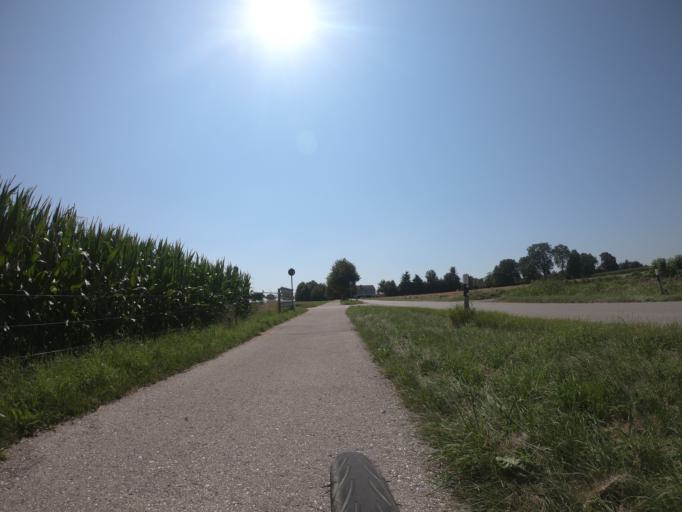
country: DE
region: Bavaria
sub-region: Upper Bavaria
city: Fuerstenfeldbruck
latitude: 48.1558
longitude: 11.2595
